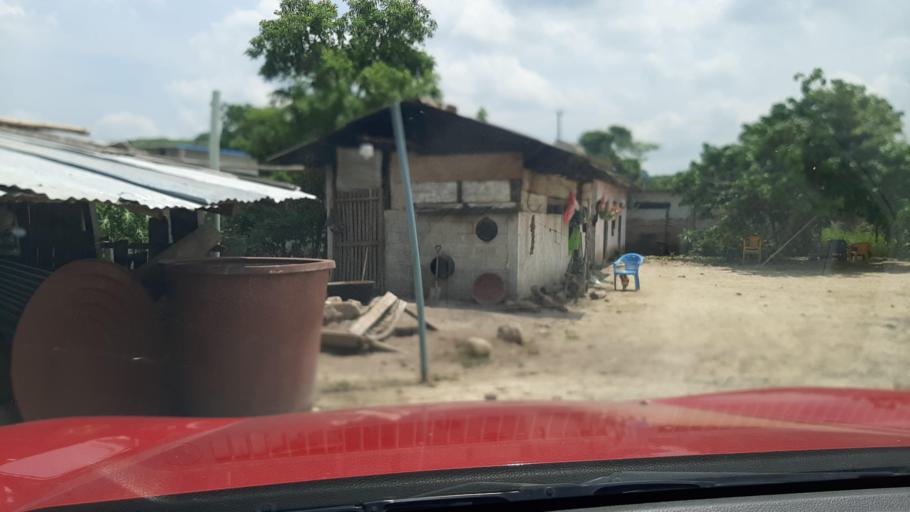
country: MX
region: Veracruz
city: Papantla de Olarte
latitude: 20.4474
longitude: -97.2456
